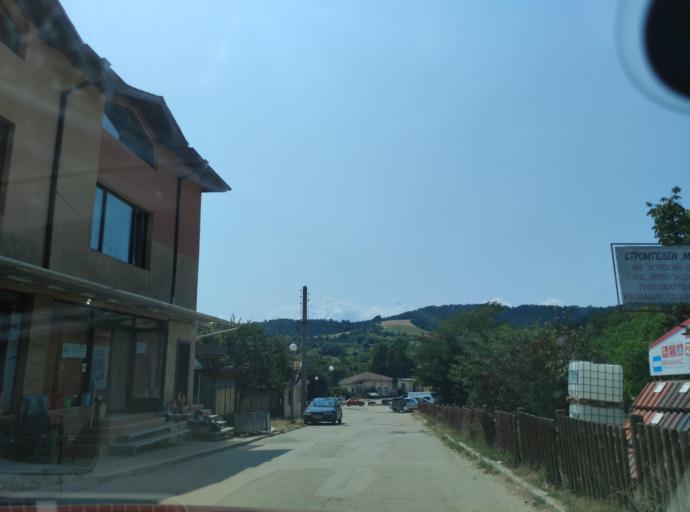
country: BG
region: Blagoevgrad
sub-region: Obshtina Belitsa
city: Belitsa
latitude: 41.9476
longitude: 23.5627
